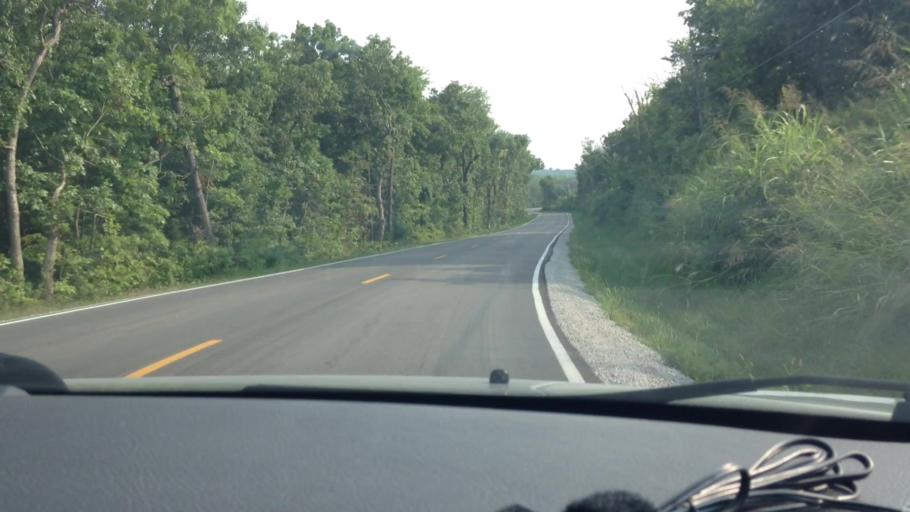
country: US
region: Missouri
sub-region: Platte County
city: Platte City
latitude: 39.3892
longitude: -94.7796
